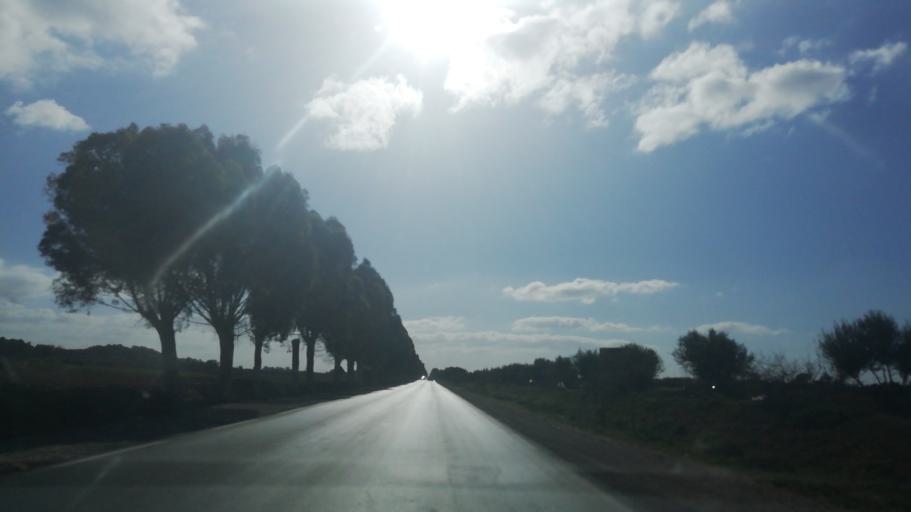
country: DZ
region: Mostaganem
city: Mostaganem
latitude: 35.9863
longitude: 0.2880
